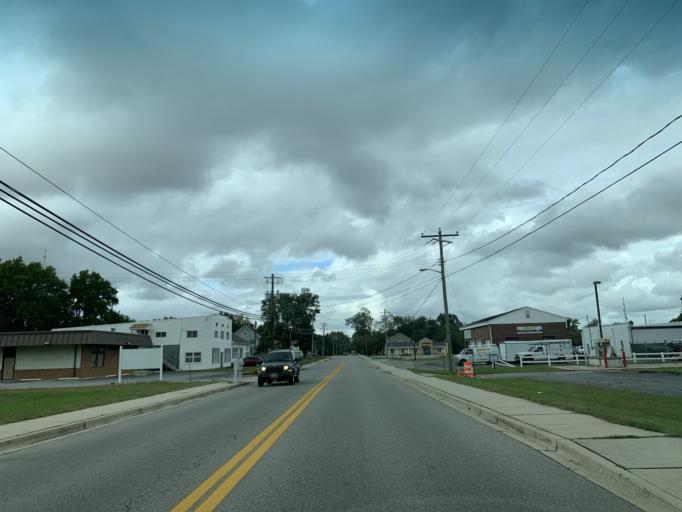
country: US
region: Maryland
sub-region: Caroline County
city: Denton
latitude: 38.8785
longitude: -75.8279
